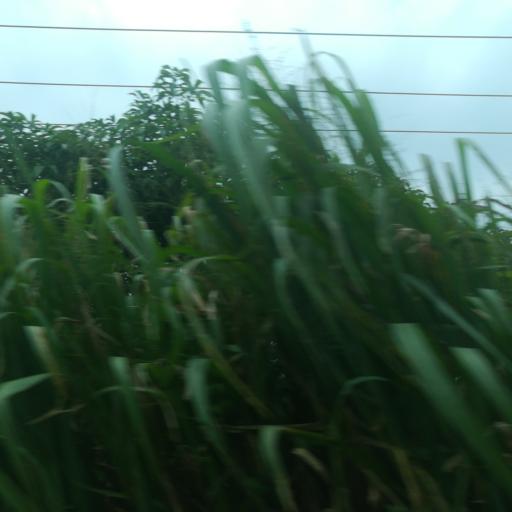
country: NG
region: Lagos
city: Ejirin
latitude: 6.6594
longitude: 3.8057
